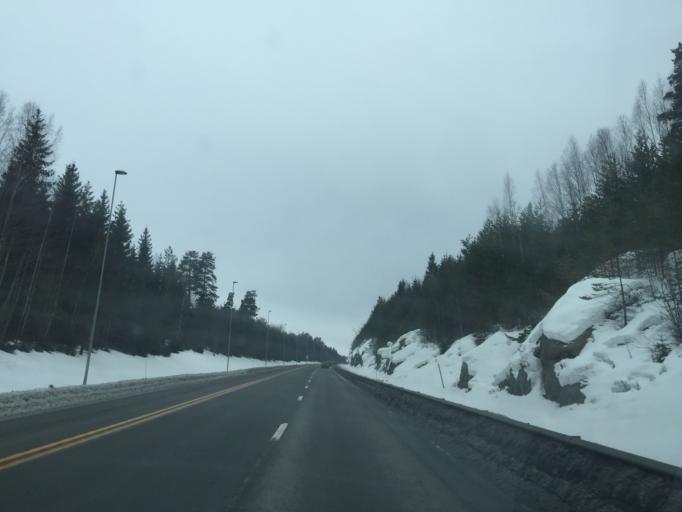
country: NO
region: Hedmark
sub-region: Loten
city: Loten
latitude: 60.7383
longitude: 11.3000
